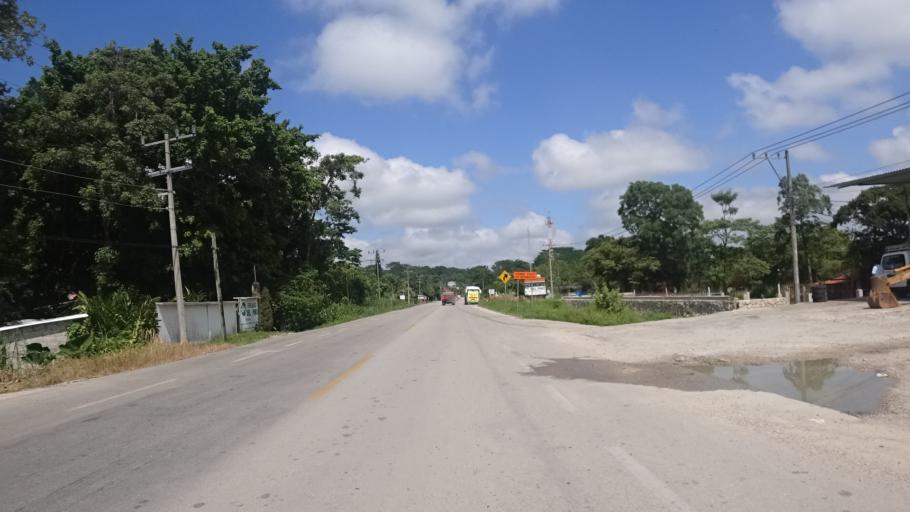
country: MX
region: Chiapas
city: Palenque
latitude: 17.4931
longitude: -91.9841
